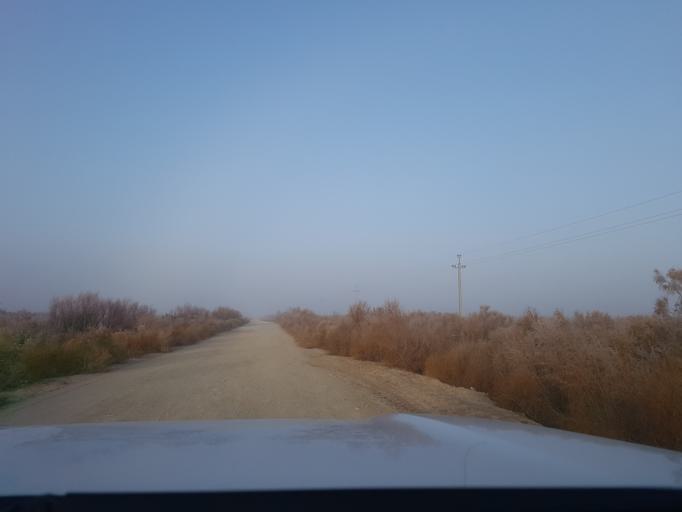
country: TM
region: Dasoguz
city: Koeneuergench
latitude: 41.8477
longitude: 58.3565
